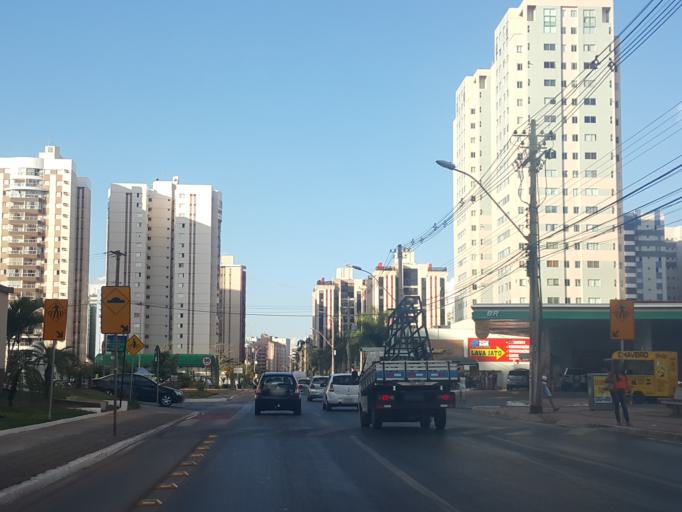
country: BR
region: Federal District
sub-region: Brasilia
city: Brasilia
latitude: -15.8399
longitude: -48.0204
